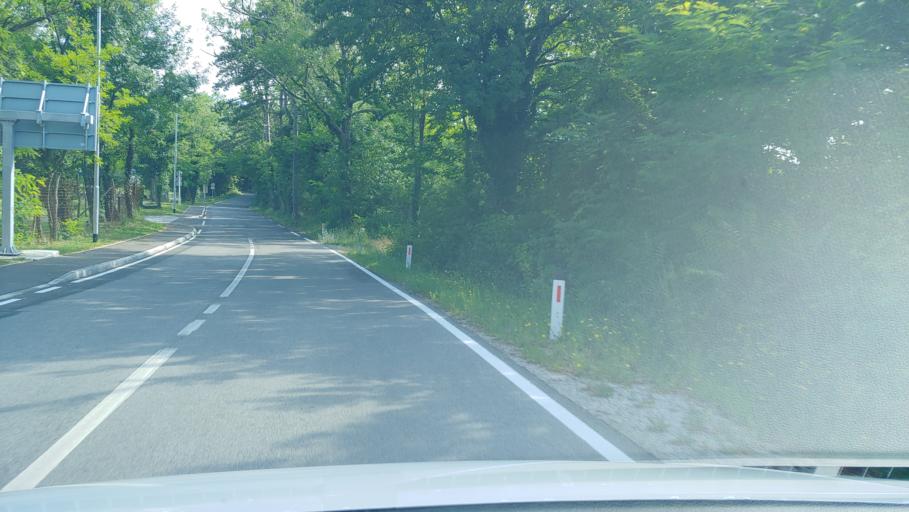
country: SI
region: Komen
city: Komen
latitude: 45.8218
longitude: 13.7526
